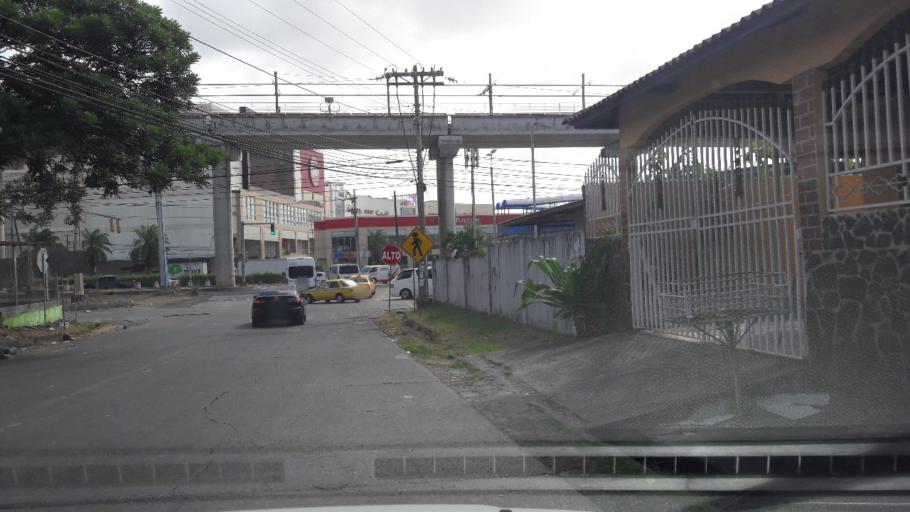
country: PA
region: Panama
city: San Miguelito
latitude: 9.0514
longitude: -79.5103
